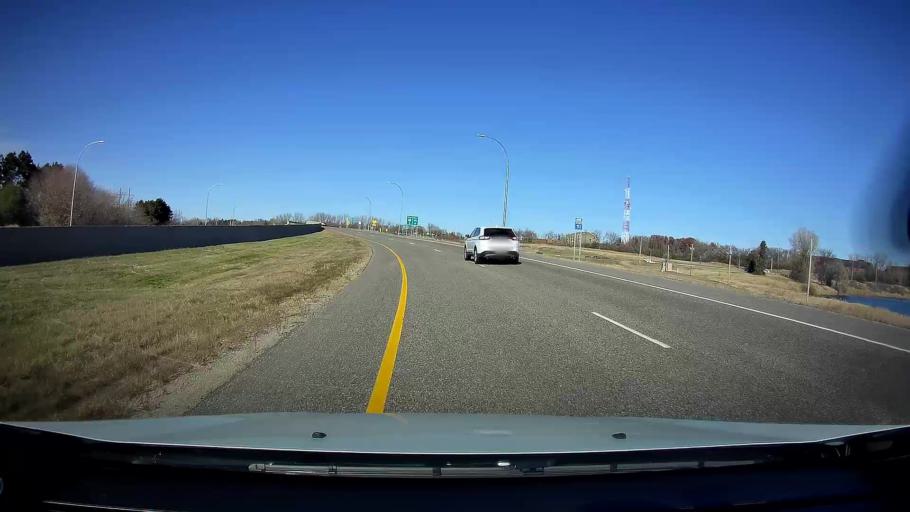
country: US
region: Minnesota
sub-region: Ramsey County
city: Arden Hills
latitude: 45.0588
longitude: -93.1571
